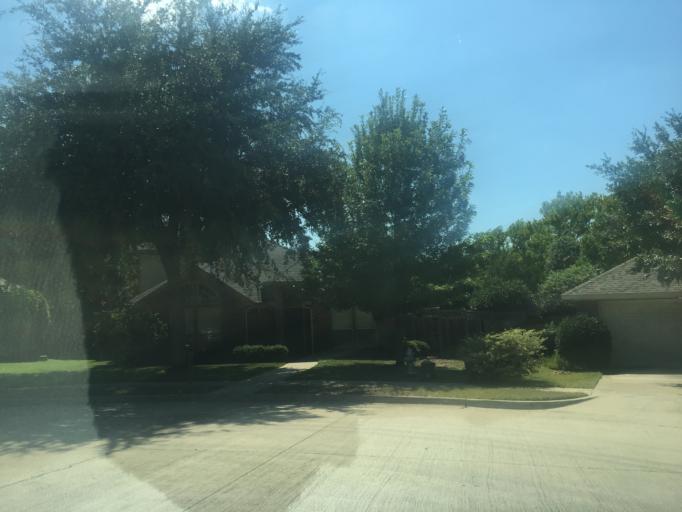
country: US
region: Texas
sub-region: Denton County
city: Lewisville
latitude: 33.0150
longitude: -97.0031
